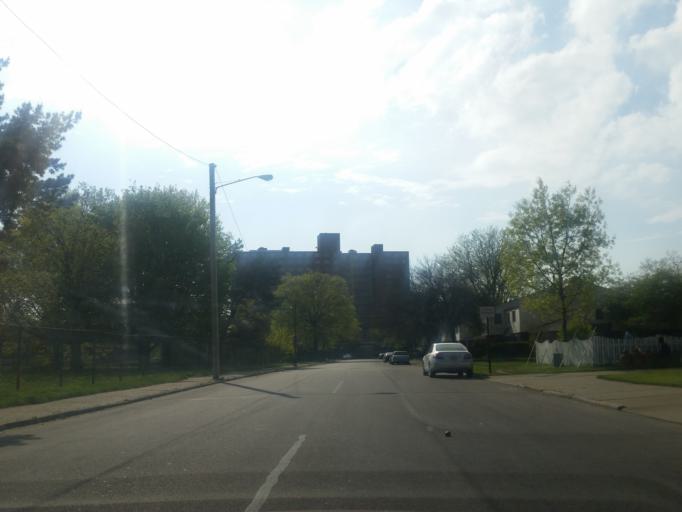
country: US
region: Ohio
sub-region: Cuyahoga County
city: Cleveland
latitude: 41.4955
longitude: -81.6638
